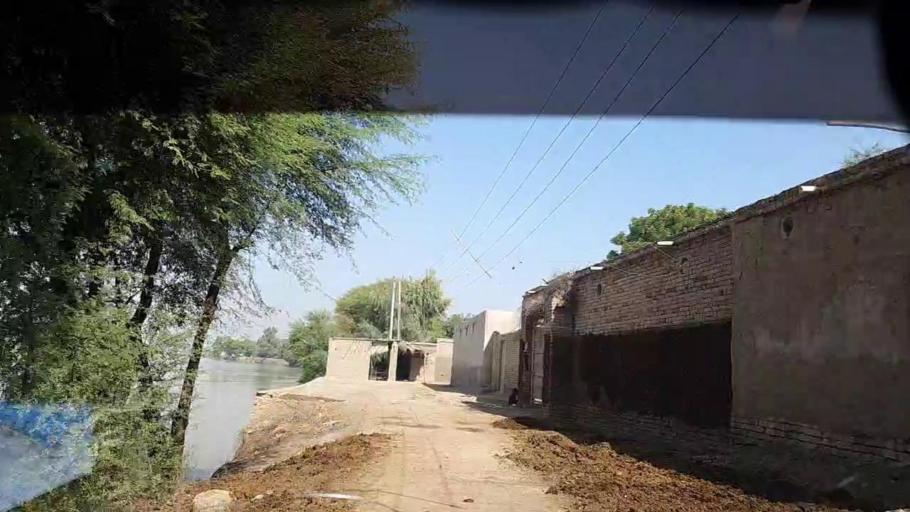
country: PK
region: Sindh
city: Naudero
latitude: 27.6687
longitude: 68.3782
